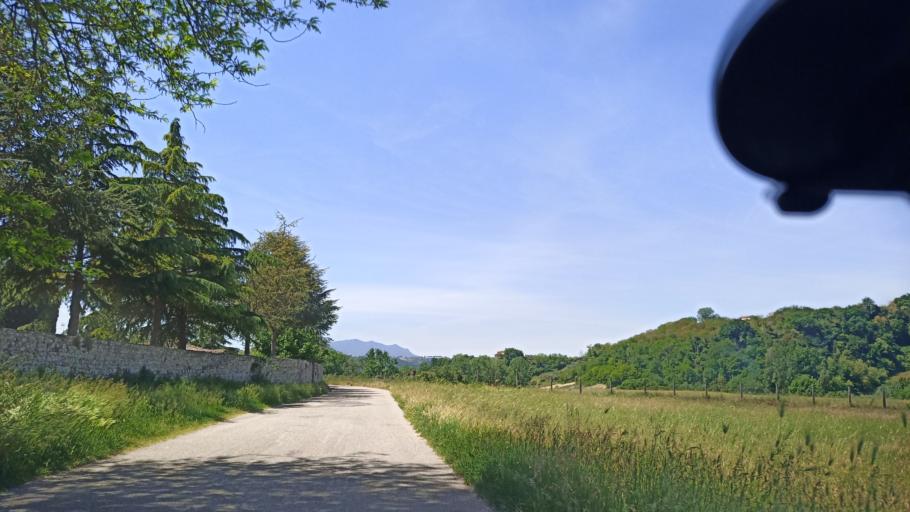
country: IT
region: Latium
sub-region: Provincia di Rieti
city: Tarano
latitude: 42.3322
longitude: 12.6047
